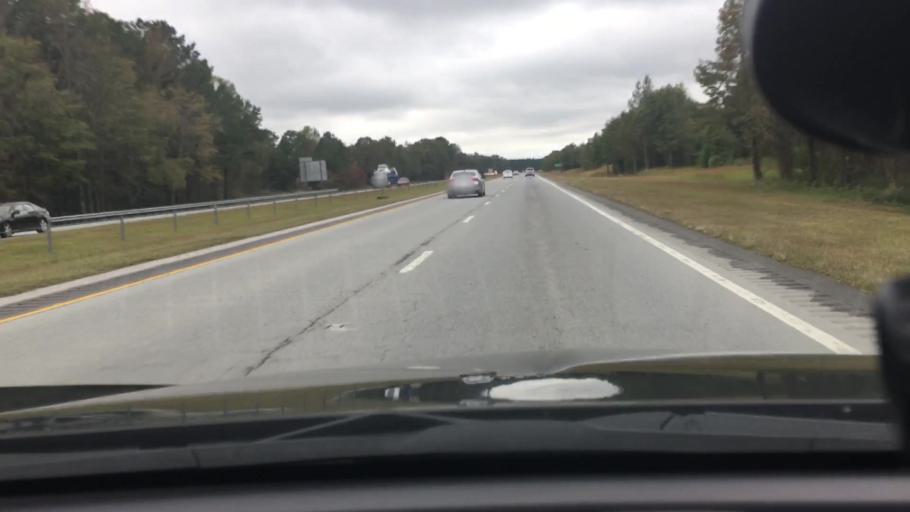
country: US
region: North Carolina
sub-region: Pitt County
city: Farmville
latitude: 35.6192
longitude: -77.6892
